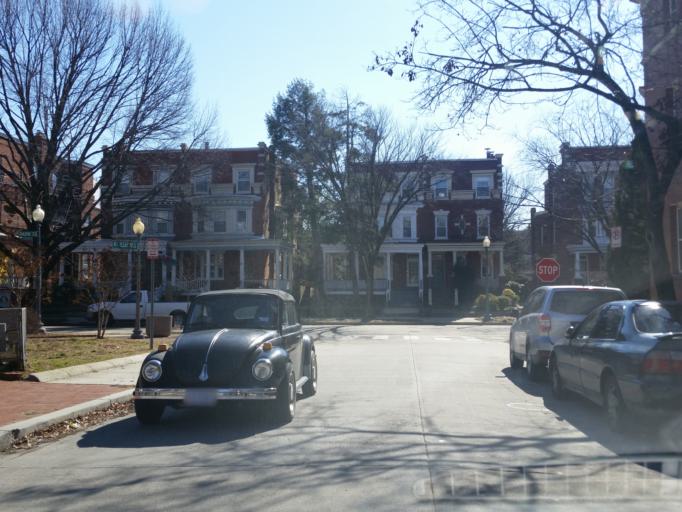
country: US
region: Washington, D.C.
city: Washington, D.C.
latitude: 38.9329
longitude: -77.0400
